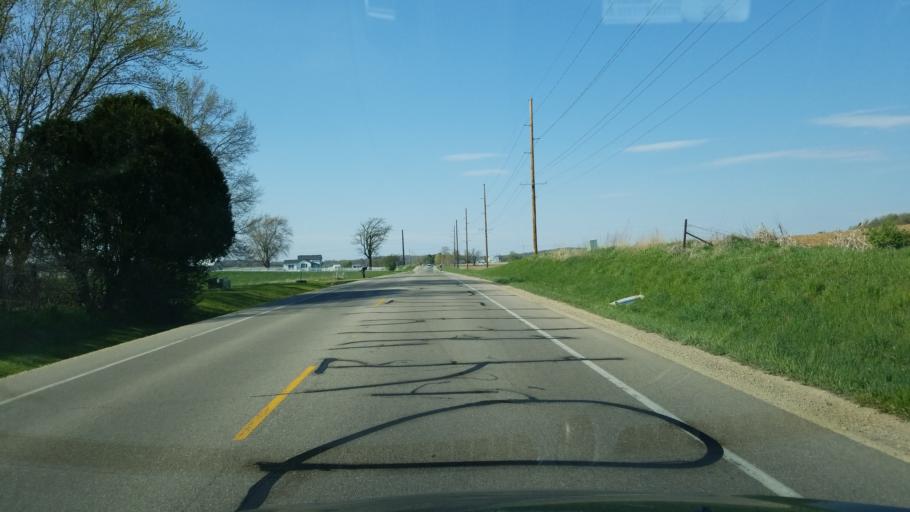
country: US
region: Wisconsin
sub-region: Dane County
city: Fitchburg
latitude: 42.9325
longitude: -89.4379
